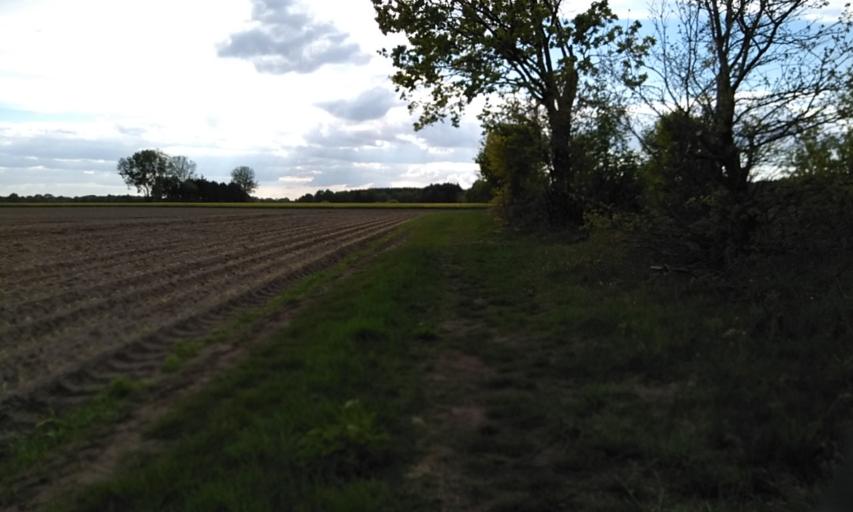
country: DE
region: Lower Saxony
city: Apensen
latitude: 53.4405
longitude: 9.6039
